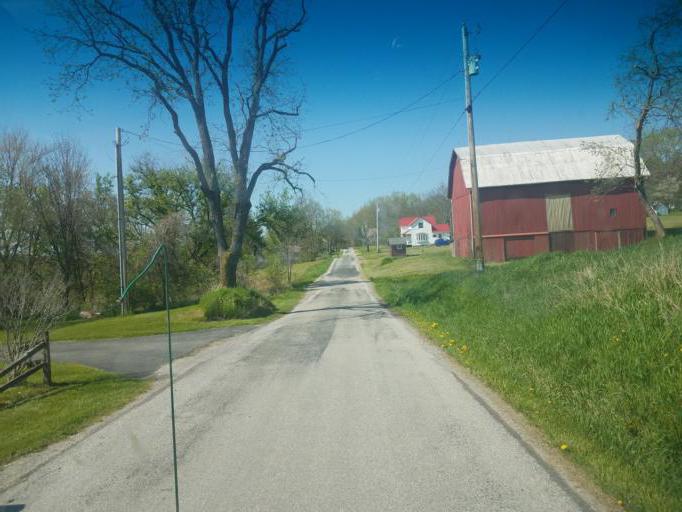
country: US
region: Ohio
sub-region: Medina County
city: Lodi
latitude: 40.9644
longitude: -82.0247
